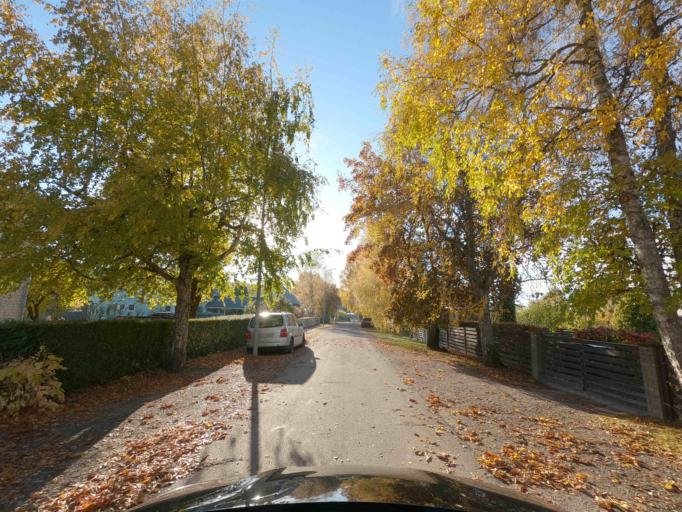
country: EE
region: Raplamaa
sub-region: Kohila vald
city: Kohila
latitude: 59.1621
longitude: 24.7686
